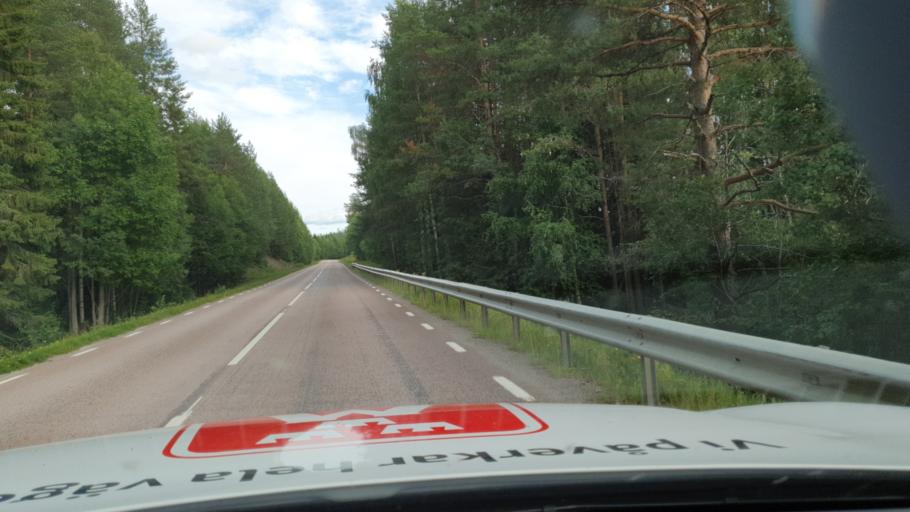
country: SE
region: Vaesternorrland
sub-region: Solleftea Kommun
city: As
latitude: 63.5970
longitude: 16.2676
